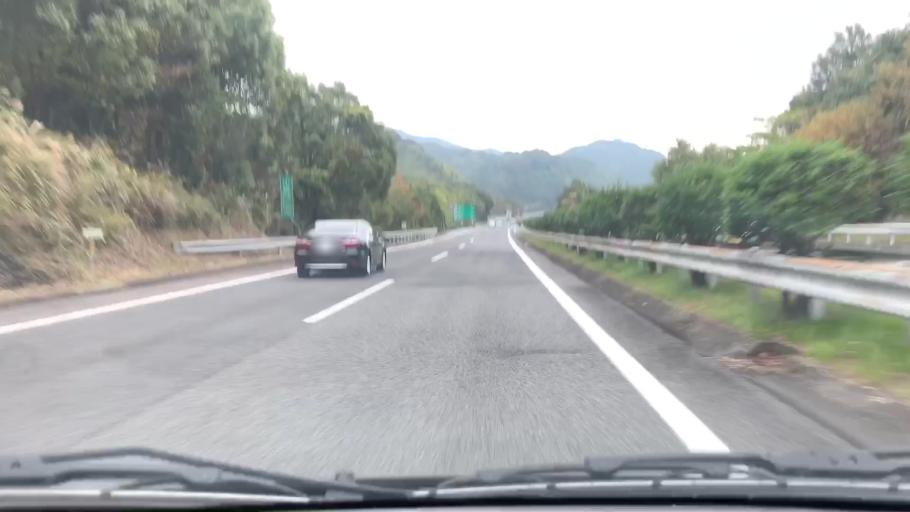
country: JP
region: Saga Prefecture
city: Saga-shi
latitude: 33.2926
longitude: 130.1676
